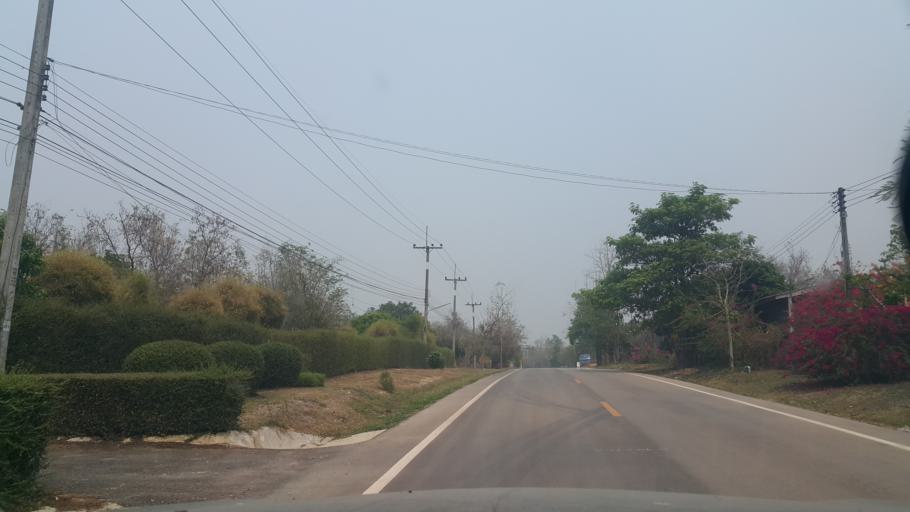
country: TH
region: Lampang
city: Hang Chat
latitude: 18.2322
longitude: 99.2314
